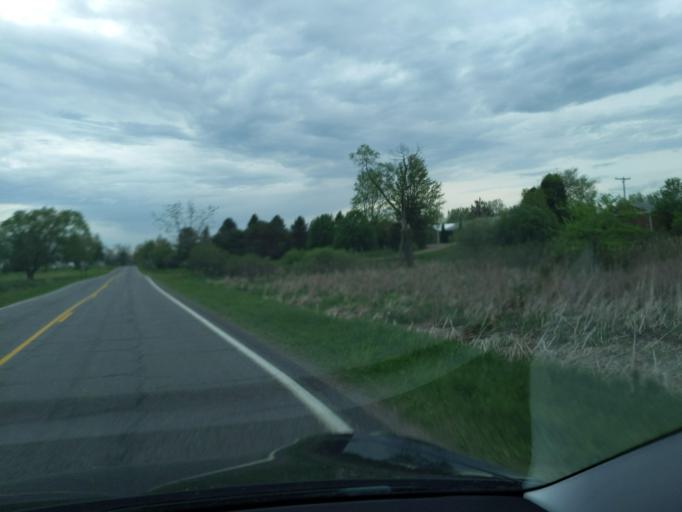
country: US
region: Michigan
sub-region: Ingham County
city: Stockbridge
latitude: 42.4542
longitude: -84.2584
